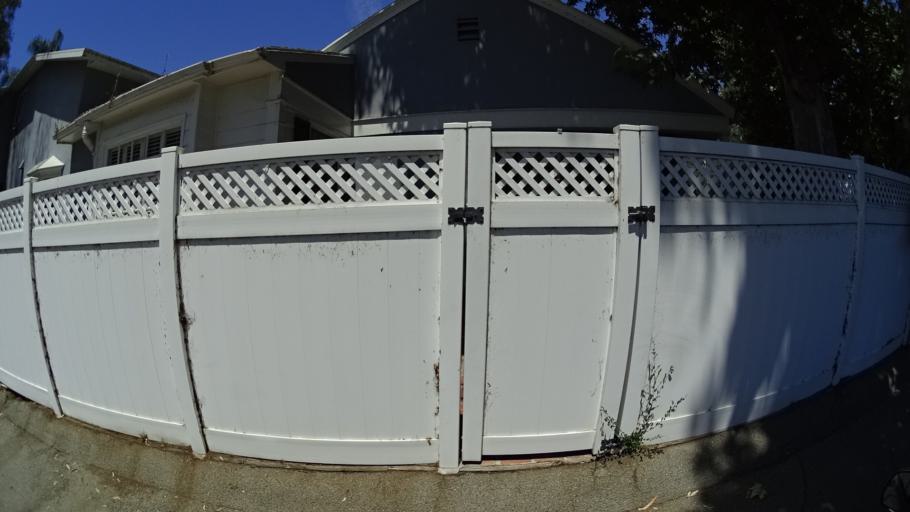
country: US
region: California
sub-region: Los Angeles County
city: Universal City
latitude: 34.1497
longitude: -118.3311
